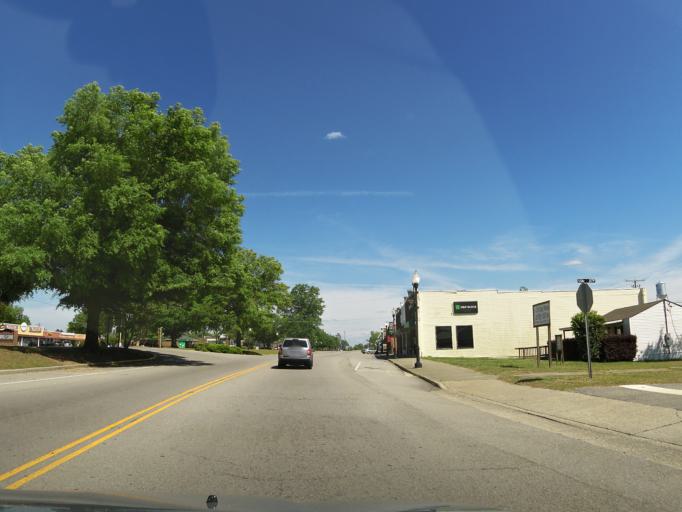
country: US
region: South Carolina
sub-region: Barnwell County
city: Williston
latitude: 33.4026
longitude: -81.4243
